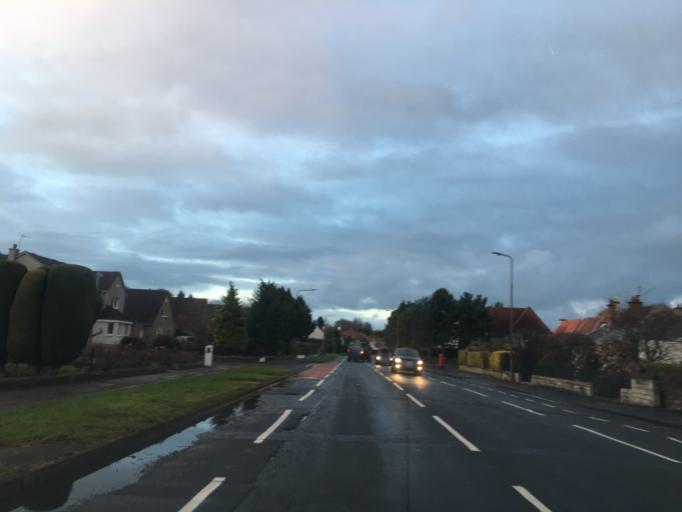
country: GB
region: Scotland
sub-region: Edinburgh
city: Colinton
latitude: 55.9586
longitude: -3.2689
